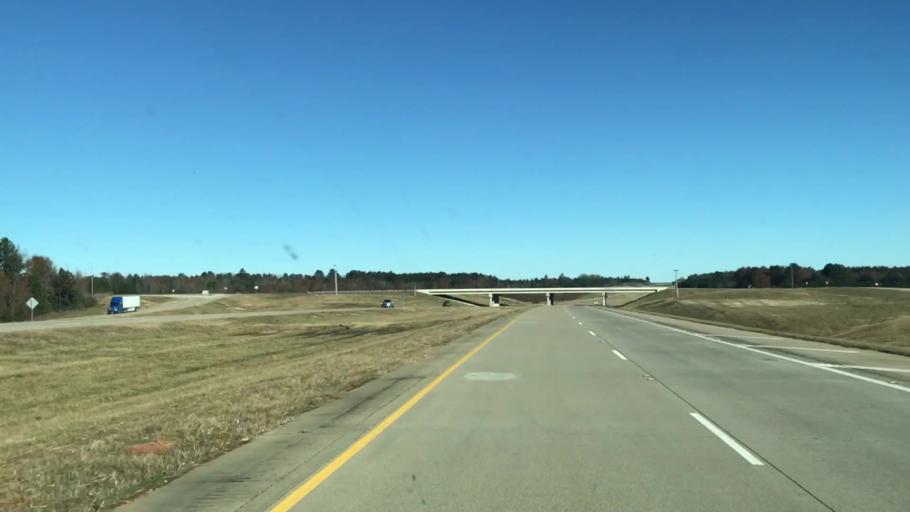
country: US
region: Louisiana
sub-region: Caddo Parish
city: Vivian
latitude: 32.9934
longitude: -93.9102
